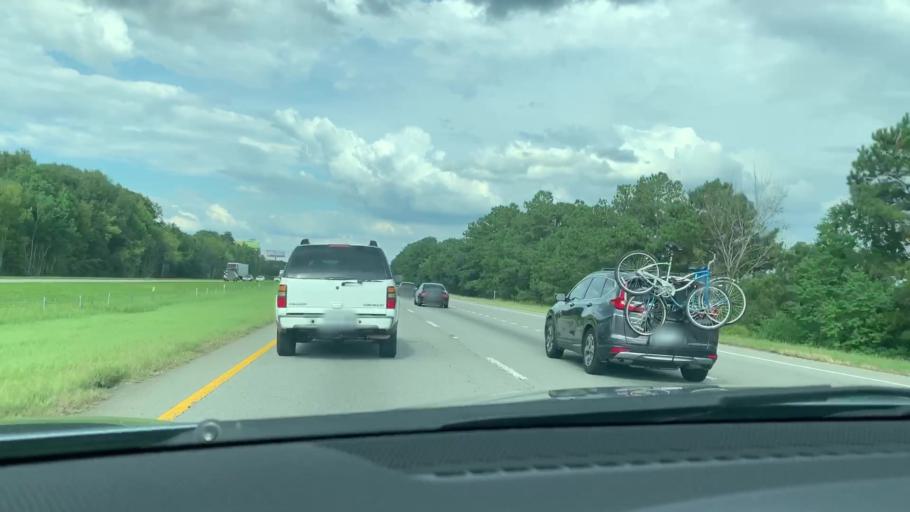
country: US
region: South Carolina
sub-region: Jasper County
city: Ridgeland
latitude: 32.5828
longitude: -80.9276
